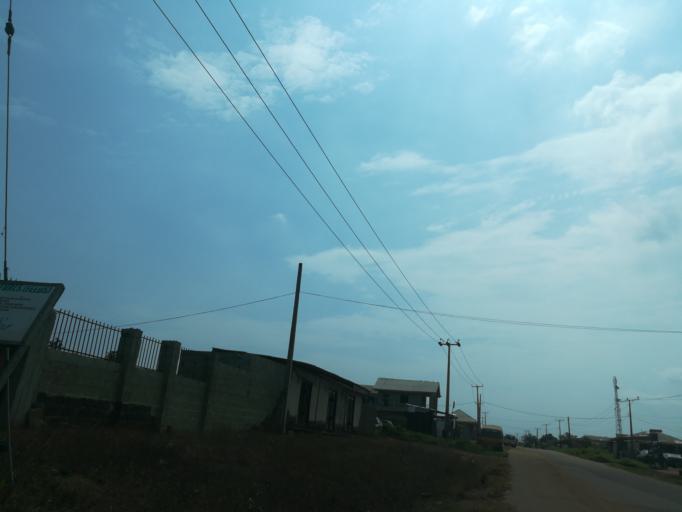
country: NG
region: Lagos
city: Ikorodu
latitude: 6.6011
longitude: 3.6276
